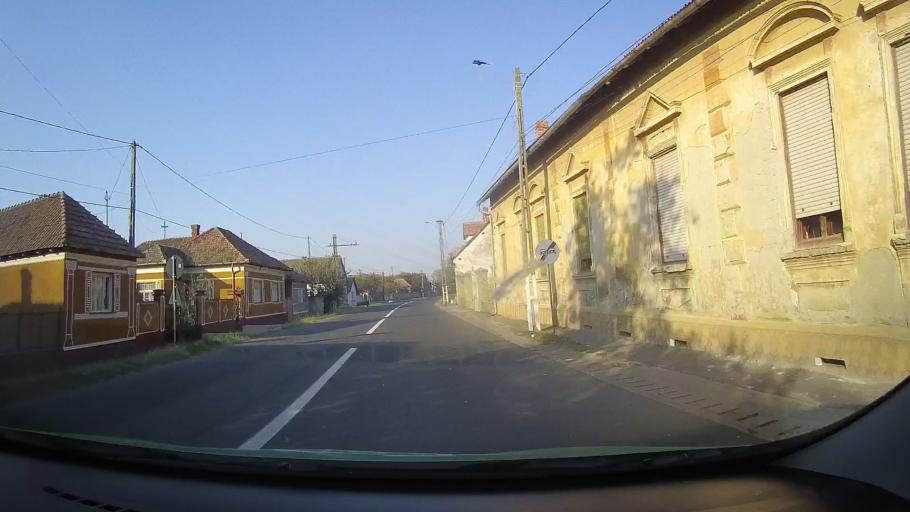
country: RO
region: Arad
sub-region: Comuna Covasint
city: Covasint
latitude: 46.2077
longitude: 21.6097
